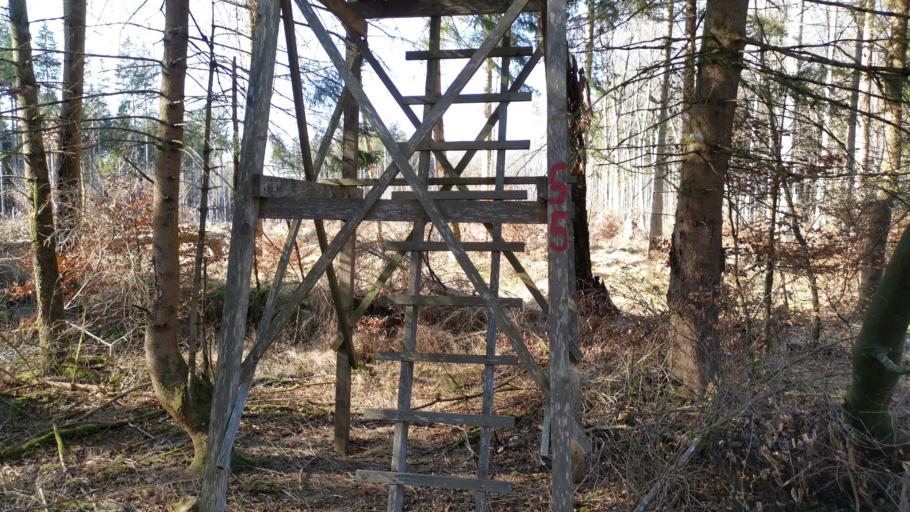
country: DE
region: Bavaria
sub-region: Upper Bavaria
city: Schaftlarn
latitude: 48.0300
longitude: 11.4445
